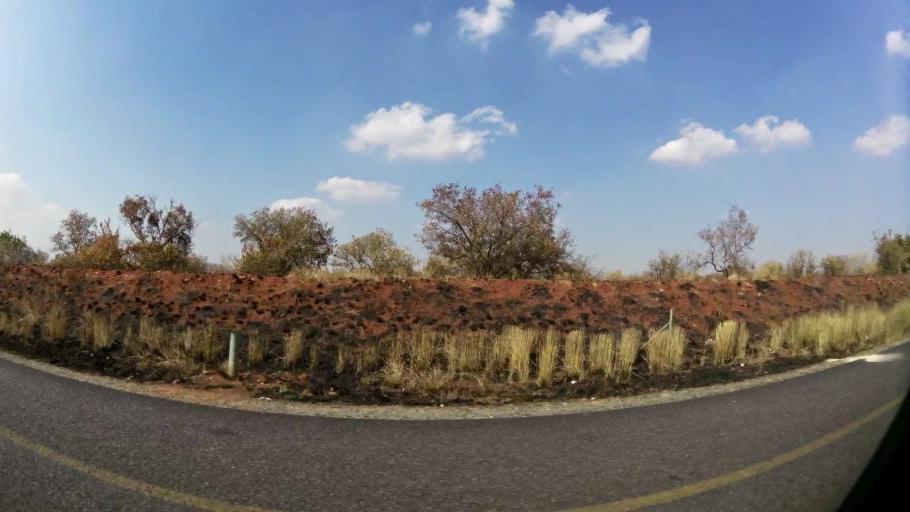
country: ZA
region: North-West
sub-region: Bojanala Platinum District Municipality
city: Rustenburg
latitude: -25.5635
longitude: 27.1432
